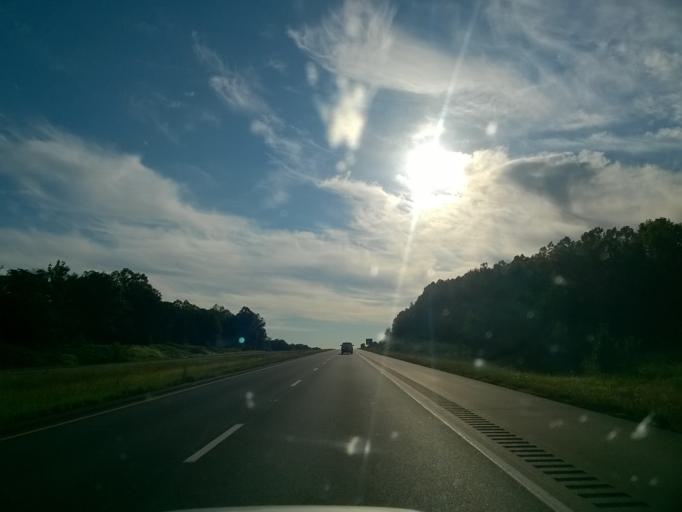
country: US
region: Indiana
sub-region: Gibson County
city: Oakland City
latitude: 38.1922
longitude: -87.3210
